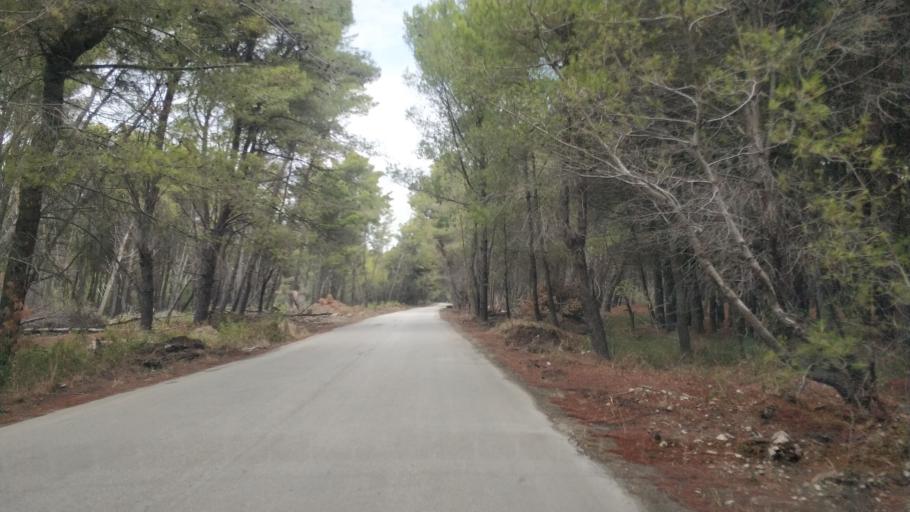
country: AL
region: Vlore
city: Vlore
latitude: 40.4827
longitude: 19.4478
